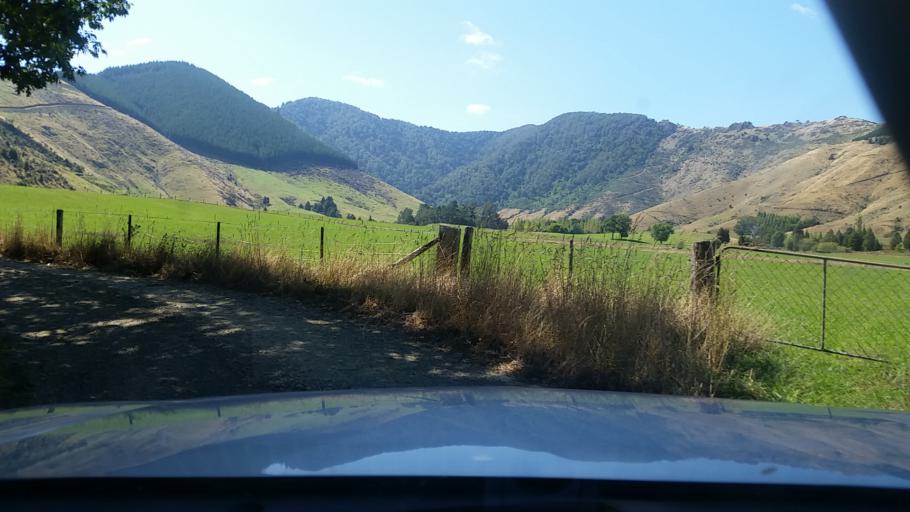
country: NZ
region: Nelson
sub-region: Nelson City
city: Nelson
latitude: -41.2486
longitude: 173.5852
